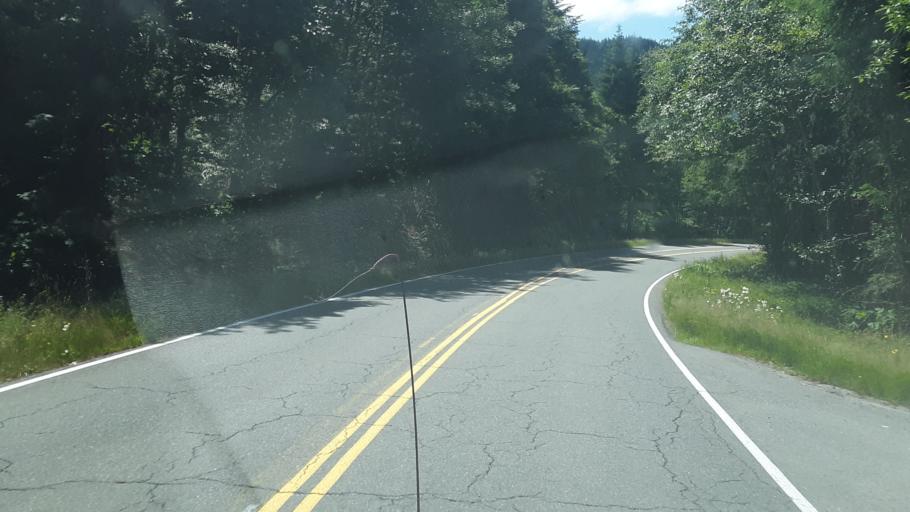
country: US
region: Washington
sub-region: Clark County
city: Yacolt
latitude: 46.0688
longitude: -122.1982
